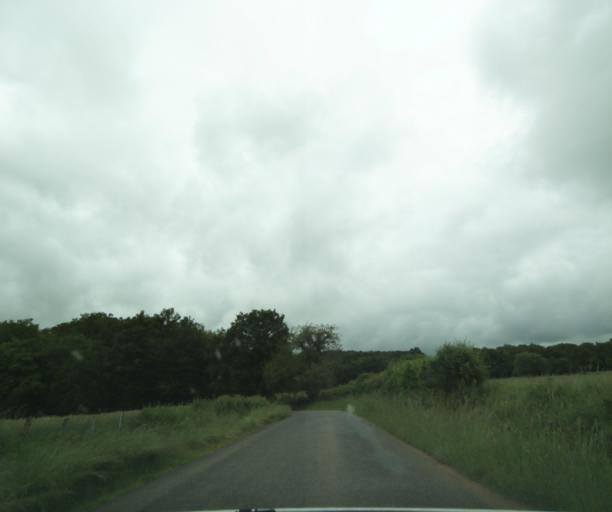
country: FR
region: Bourgogne
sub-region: Departement de Saone-et-Loire
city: Charolles
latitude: 46.4582
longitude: 4.3485
